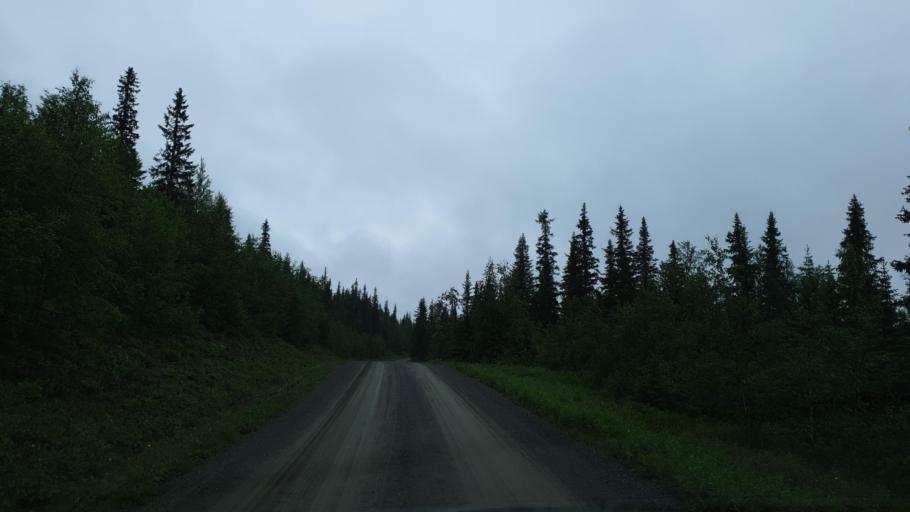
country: SE
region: Vaesterbotten
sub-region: Vilhelmina Kommun
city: Sjoberg
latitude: 65.3329
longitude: 15.9030
